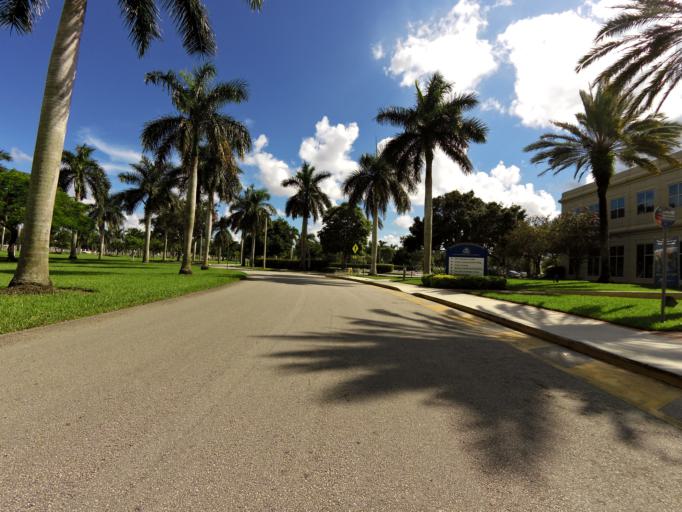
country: US
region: Florida
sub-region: Broward County
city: Davie
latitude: 26.0788
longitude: -80.2398
